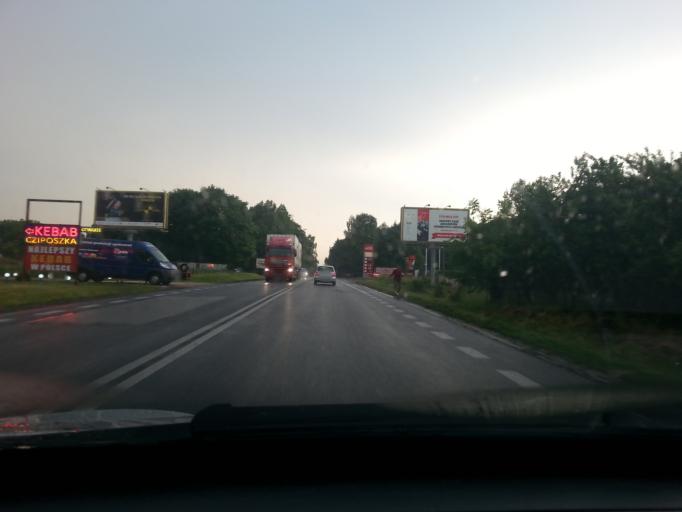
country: PL
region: Lodz Voivodeship
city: Lodz
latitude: 51.8245
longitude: 19.5186
